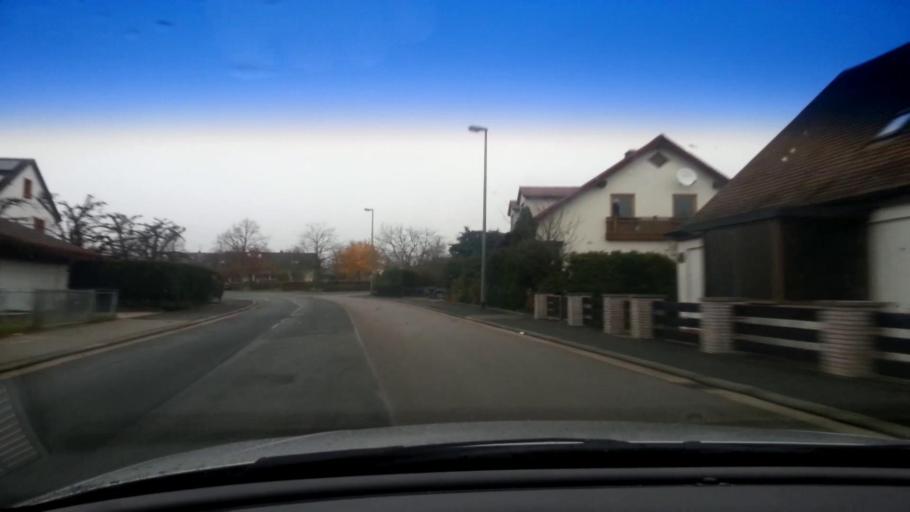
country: DE
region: Bavaria
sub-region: Upper Franconia
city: Gundelsheim
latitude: 49.9384
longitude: 10.9186
